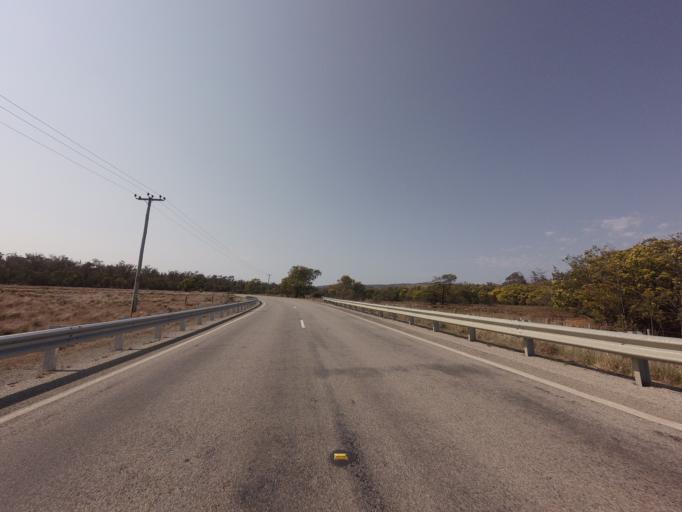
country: AU
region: Tasmania
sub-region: Northern Midlands
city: Evandale
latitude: -41.8301
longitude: 147.4913
